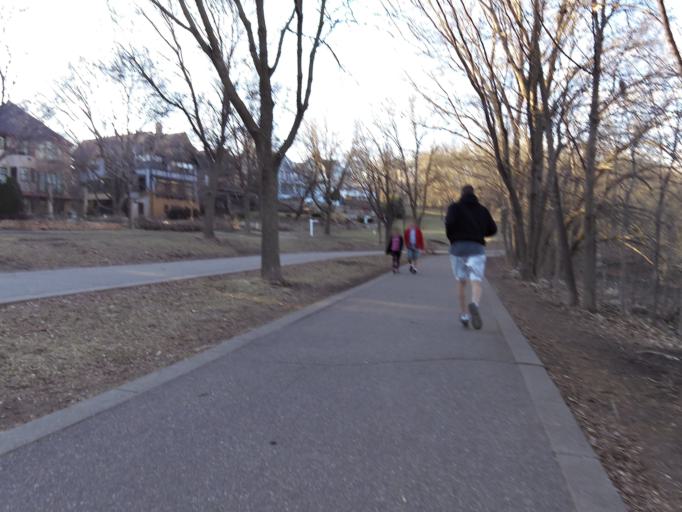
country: US
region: Minnesota
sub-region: Hennepin County
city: Saint Louis Park
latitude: 44.9184
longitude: -93.3139
